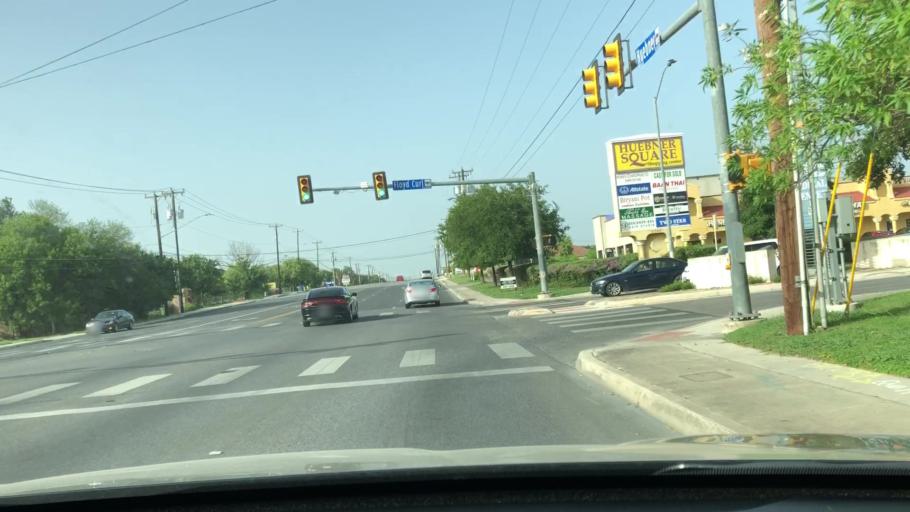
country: US
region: Texas
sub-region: Bexar County
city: Leon Valley
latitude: 29.5294
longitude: -98.5941
